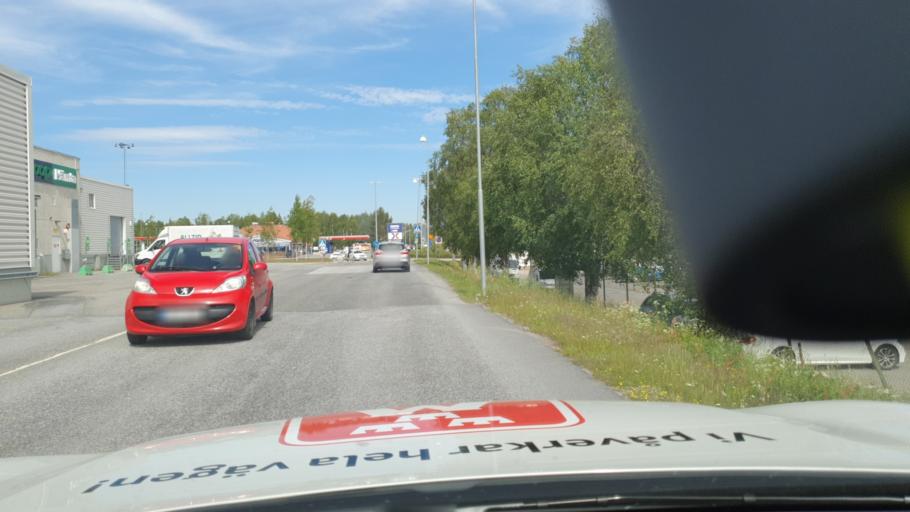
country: SE
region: Vaesterbotten
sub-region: Umea Kommun
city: Ersmark
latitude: 63.8502
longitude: 20.3015
